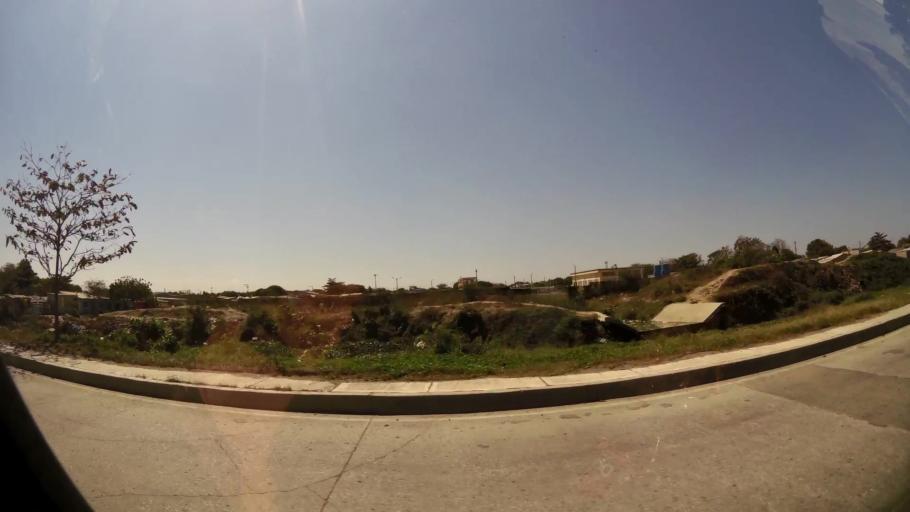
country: CO
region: Atlantico
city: Barranquilla
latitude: 10.9634
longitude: -74.7688
